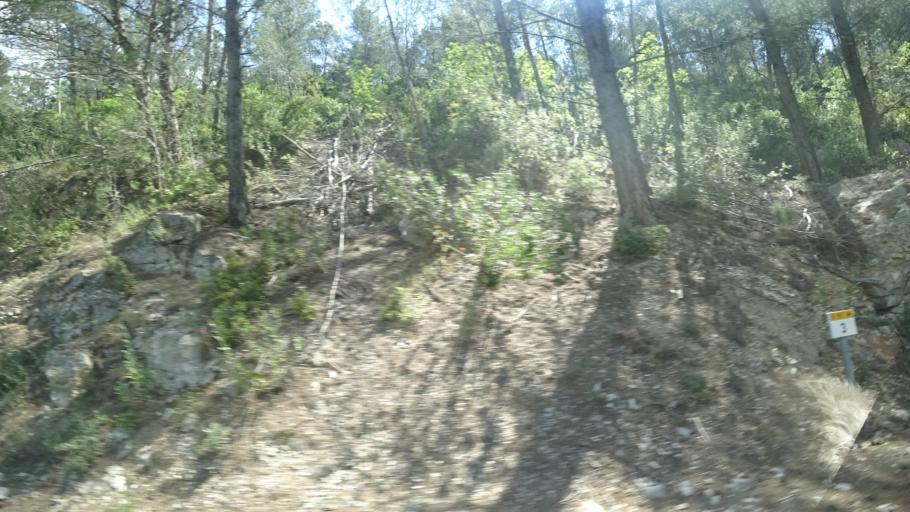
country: FR
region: Languedoc-Roussillon
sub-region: Departement de l'Herault
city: Olonzac
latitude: 43.3512
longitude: 2.7568
